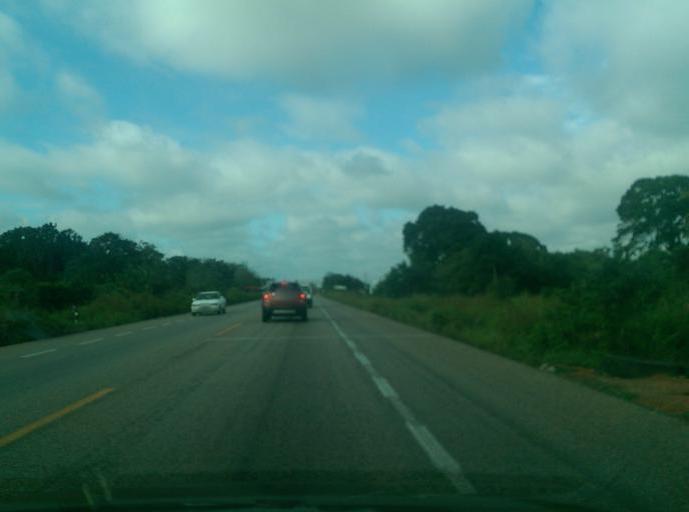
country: MX
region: Tabasco
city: Aquiles Serdan
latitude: 17.6996
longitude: -92.2565
